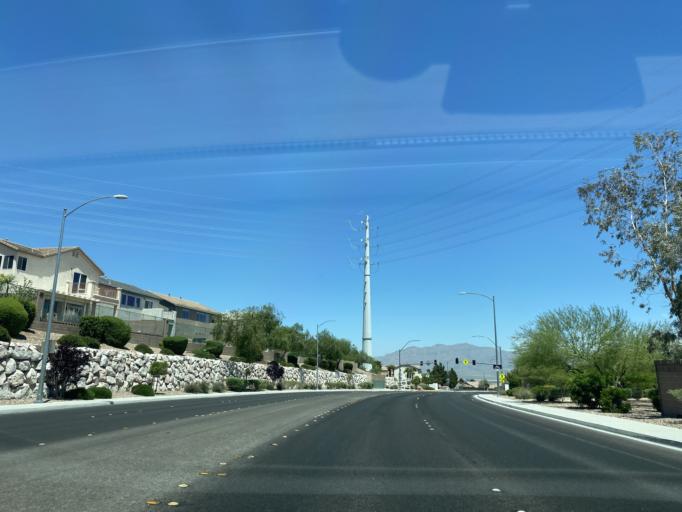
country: US
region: Nevada
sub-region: Clark County
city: Summerlin South
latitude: 36.2387
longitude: -115.3302
